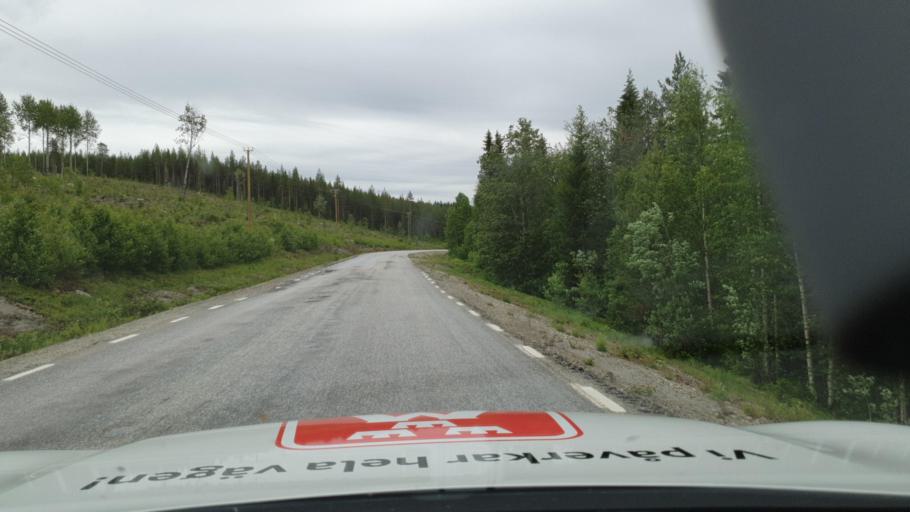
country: SE
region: Vaesterbotten
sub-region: Lycksele Kommun
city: Lycksele
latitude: 64.1041
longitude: 18.3642
